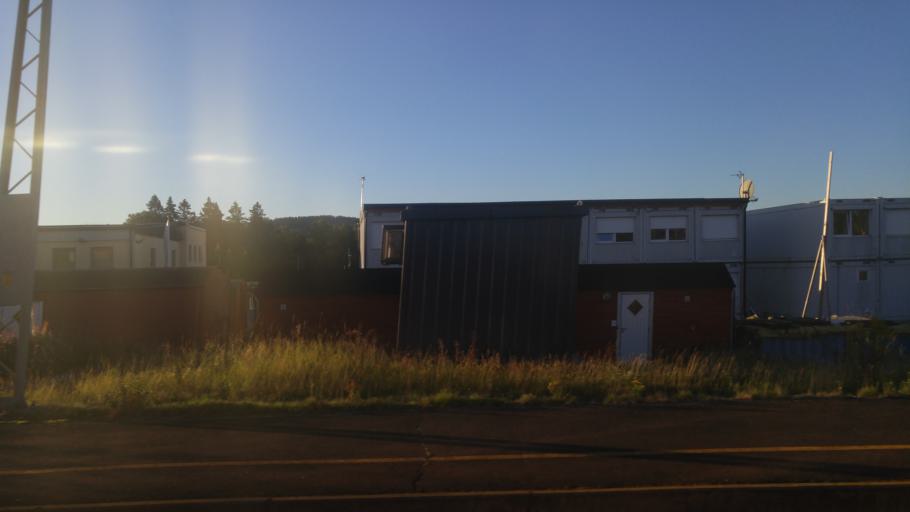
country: NO
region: Akershus
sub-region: Lorenskog
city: Kjenn
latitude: 59.9443
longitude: 10.8729
